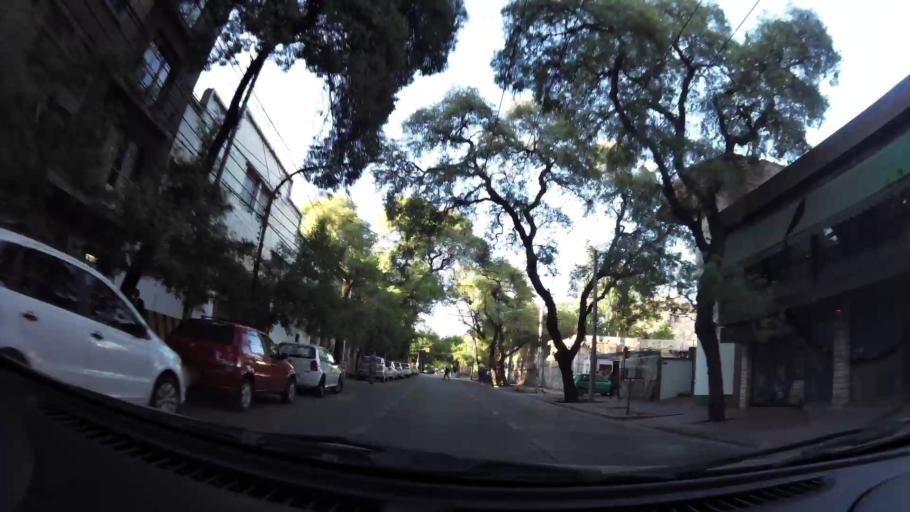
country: AR
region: Mendoza
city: Mendoza
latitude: -32.8958
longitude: -68.8422
